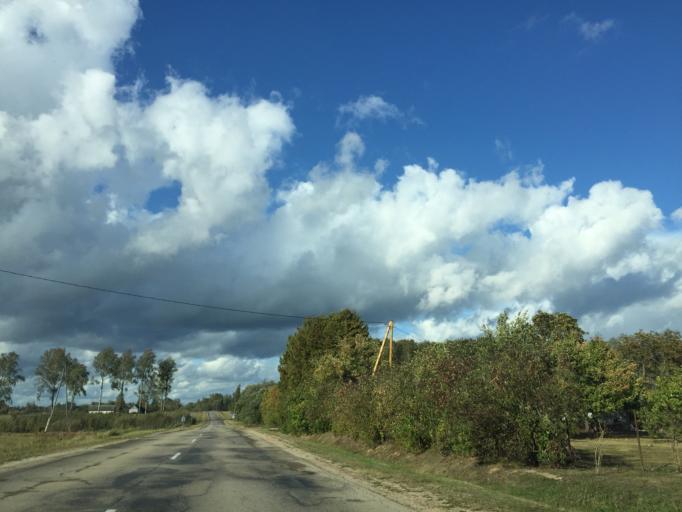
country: LV
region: Malpils
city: Malpils
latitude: 56.9349
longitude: 24.9322
